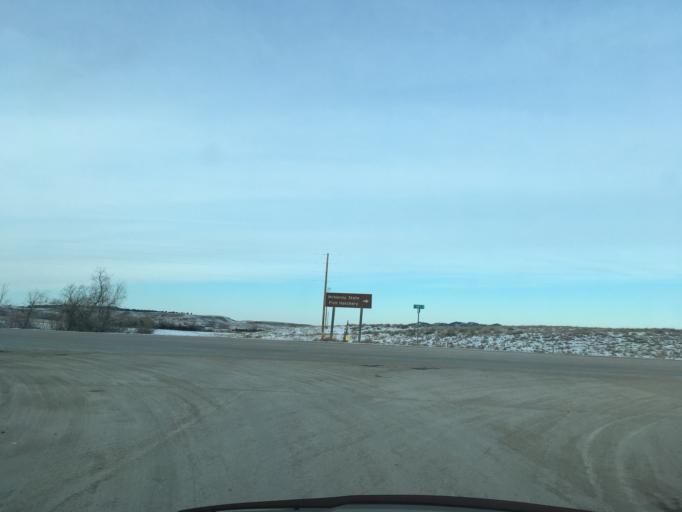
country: US
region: South Dakota
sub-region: Lawrence County
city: North Spearfish
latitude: 44.5476
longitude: -104.0119
